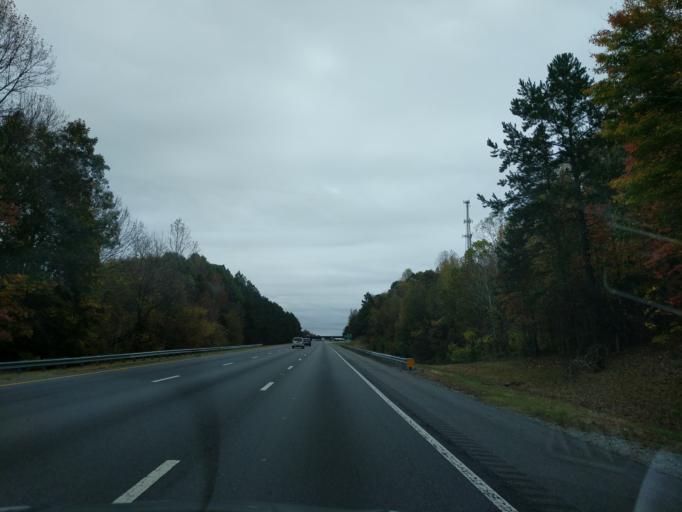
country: US
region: North Carolina
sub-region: Davidson County
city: Lexington
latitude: 35.7902
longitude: -80.2248
